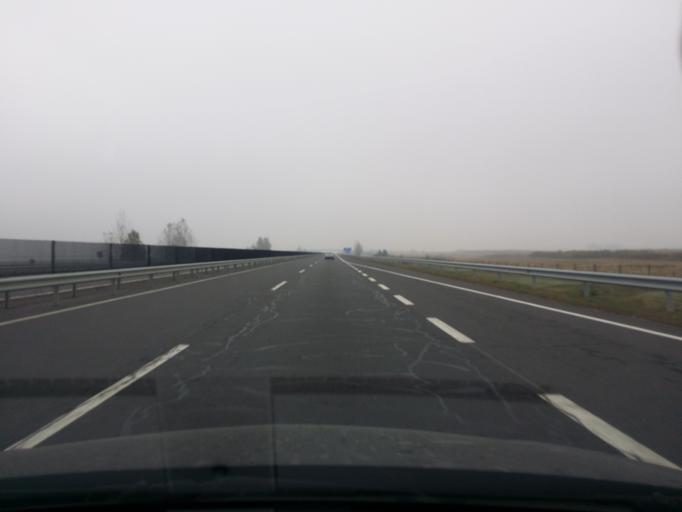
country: HU
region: Hajdu-Bihar
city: Hajdunanas
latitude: 47.8829
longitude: 21.4174
